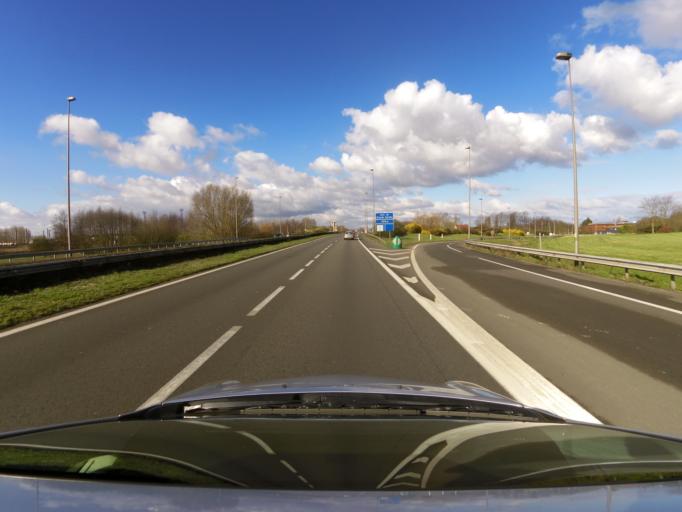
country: FR
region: Nord-Pas-de-Calais
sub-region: Departement du Nord
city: Grande-Synthe
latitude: 51.0052
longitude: 2.3158
